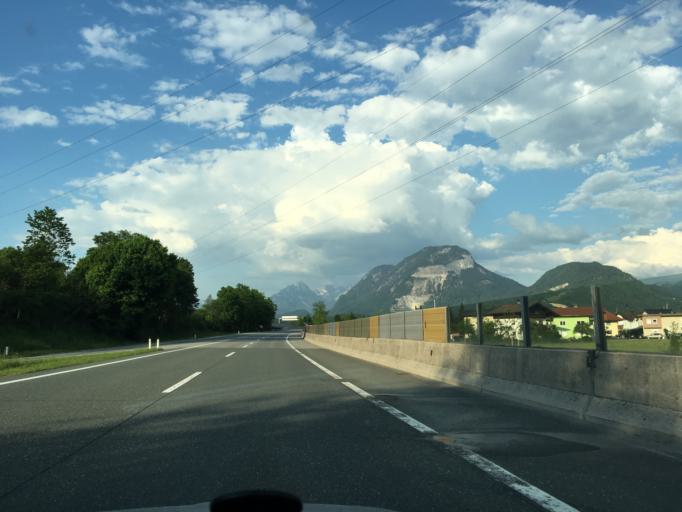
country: AT
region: Tyrol
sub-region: Politischer Bezirk Kufstein
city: Angath
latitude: 47.4943
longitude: 12.0604
